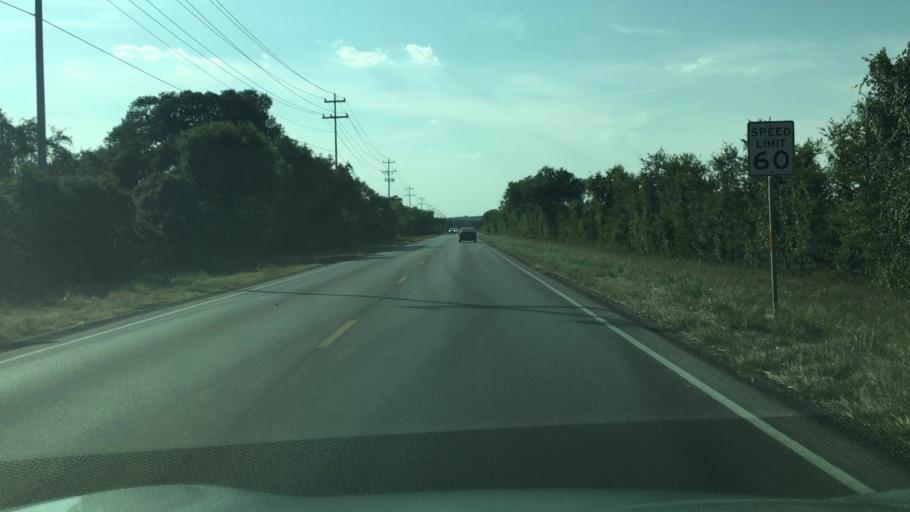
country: US
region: Texas
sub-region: Travis County
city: Shady Hollow
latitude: 30.1082
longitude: -97.9450
